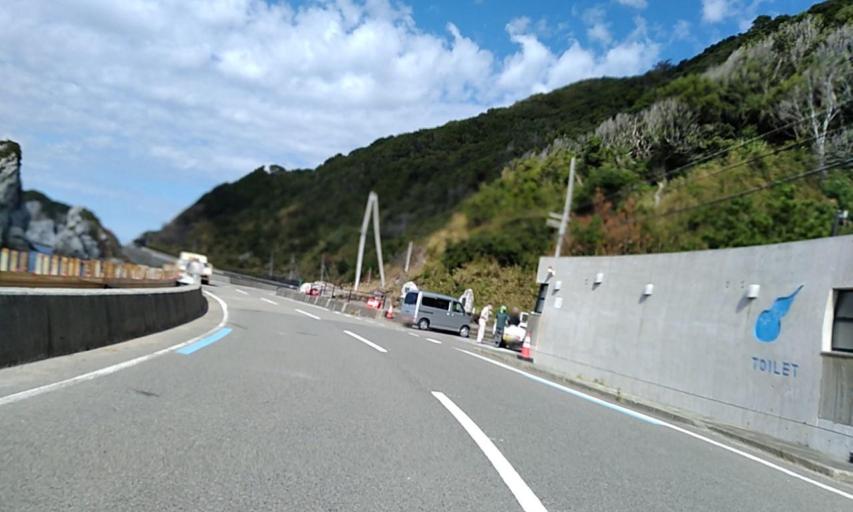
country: JP
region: Wakayama
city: Gobo
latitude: 33.9718
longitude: 135.0793
